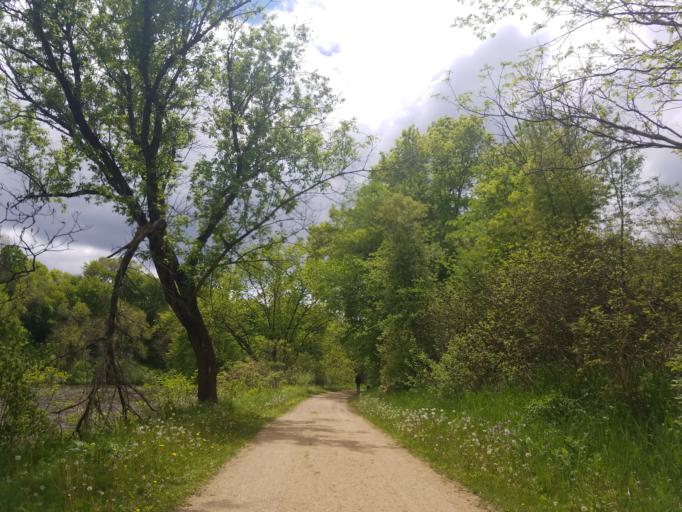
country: US
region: Wisconsin
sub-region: Dunn County
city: Menomonie
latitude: 44.8639
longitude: -91.9440
